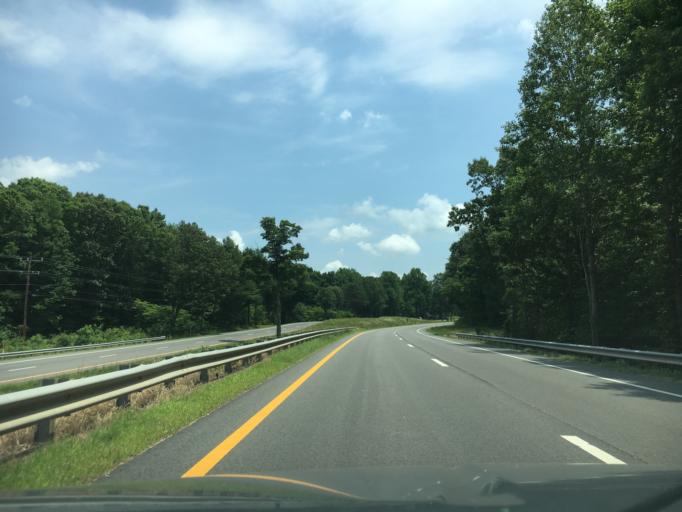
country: US
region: Virginia
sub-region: Buckingham County
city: Buckingham
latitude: 37.5467
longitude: -78.5233
